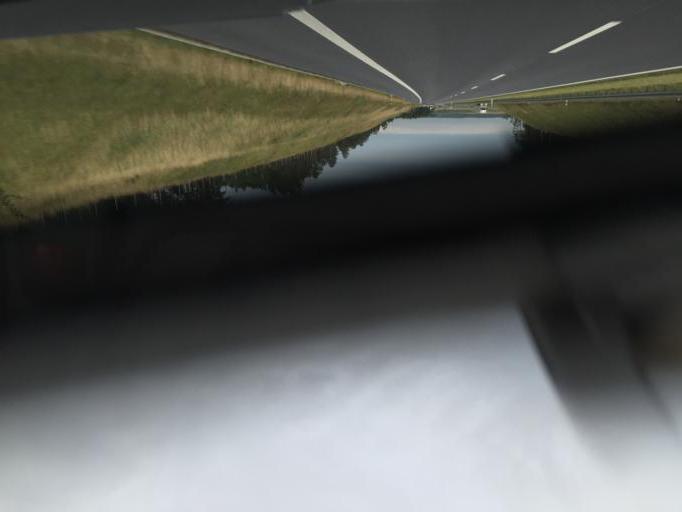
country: PL
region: Podlasie
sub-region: Powiat zambrowski
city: Rutki-Kossaki
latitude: 53.0840
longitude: 22.4627
